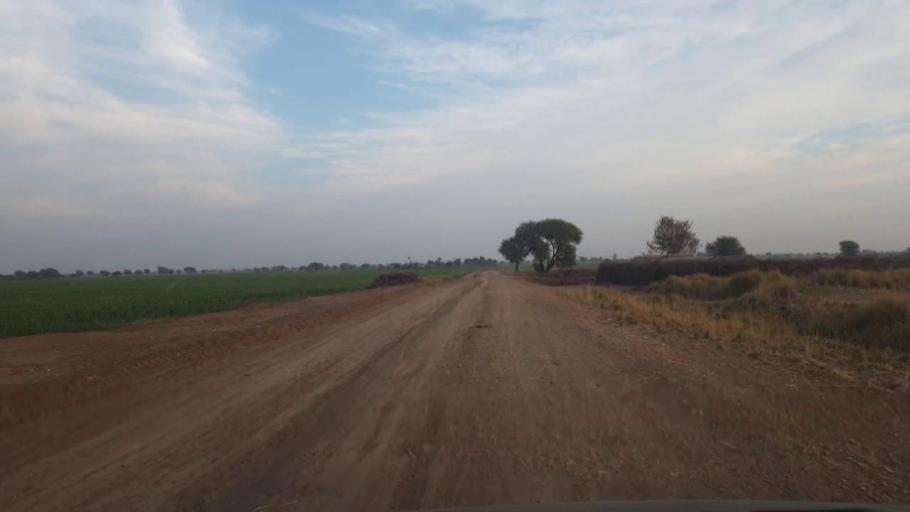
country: PK
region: Sindh
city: Shahpur Chakar
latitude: 26.0565
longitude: 68.5304
